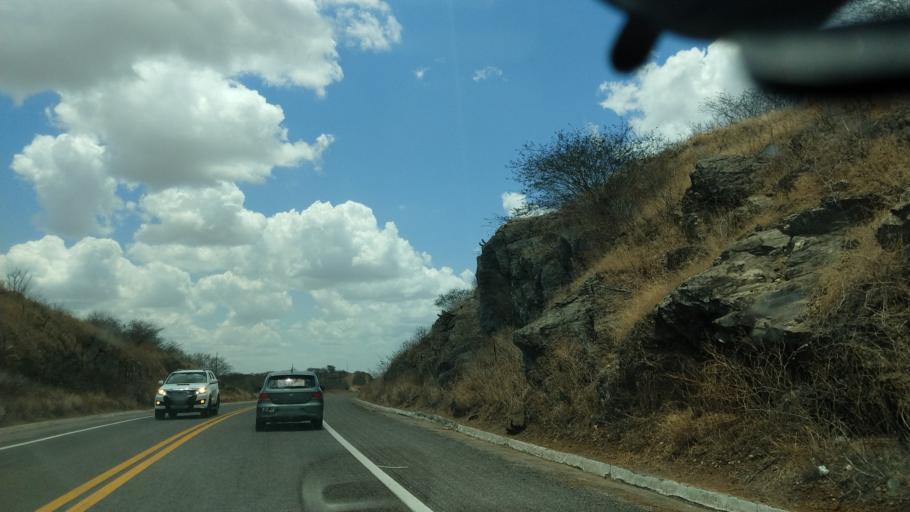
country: BR
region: Rio Grande do Norte
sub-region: Cerro Cora
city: Cerro Cora
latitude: -6.2109
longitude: -36.3021
